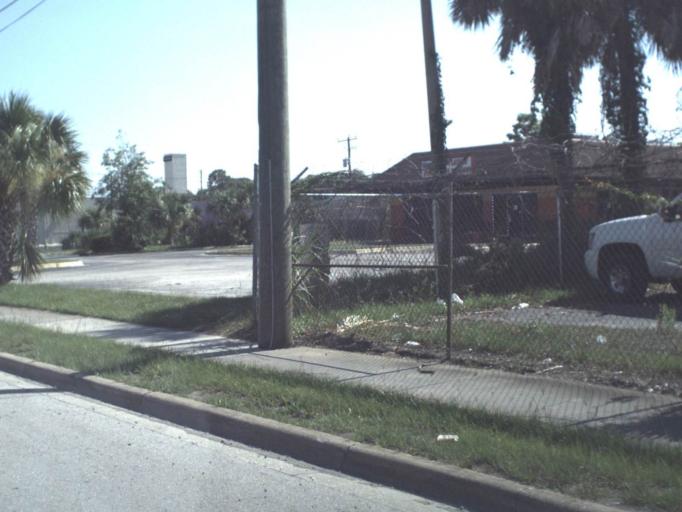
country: US
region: Florida
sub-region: Duval County
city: Jacksonville
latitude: 30.3336
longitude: -81.7311
